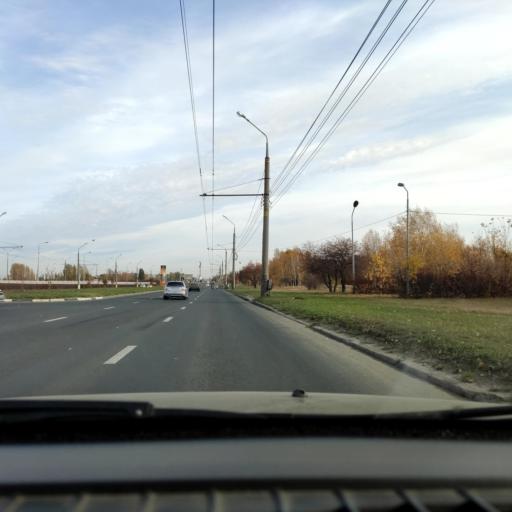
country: RU
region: Samara
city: Tol'yatti
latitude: 53.5542
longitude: 49.2763
